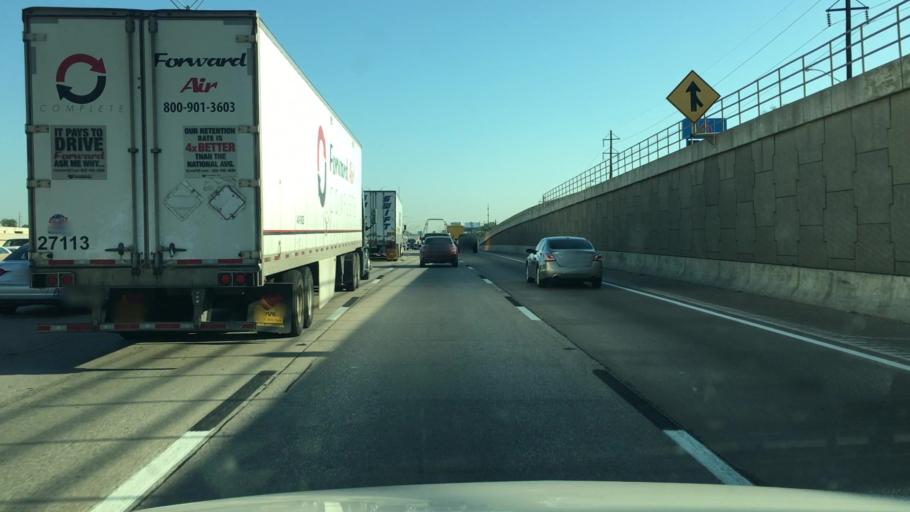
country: US
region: Texas
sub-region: Tarrant County
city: Edgecliff Village
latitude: 32.6853
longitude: -97.3205
